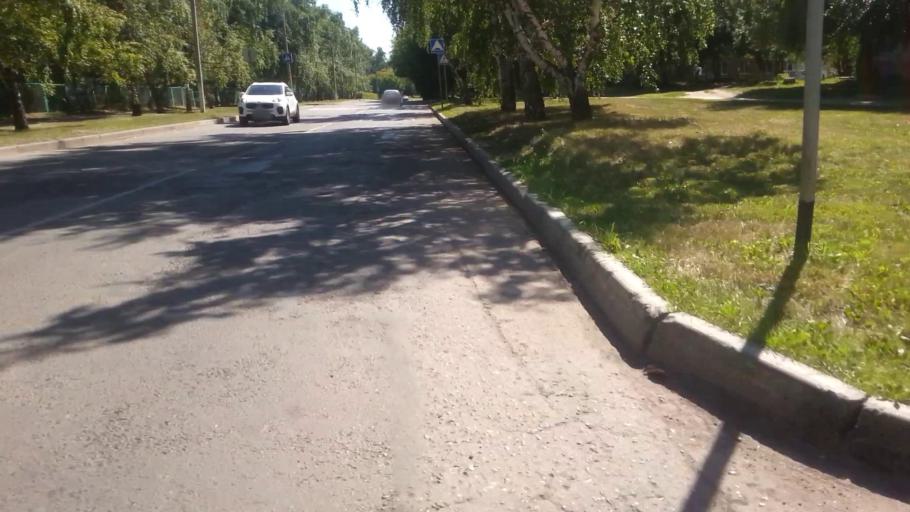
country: RU
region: Altai Krai
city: Novosilikatnyy
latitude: 53.3645
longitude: 83.6677
